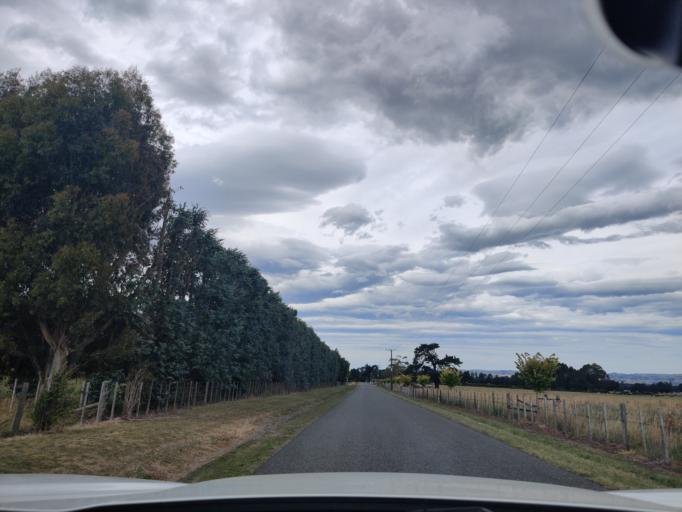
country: NZ
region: Wellington
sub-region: Masterton District
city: Masterton
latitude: -41.0365
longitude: 175.4402
